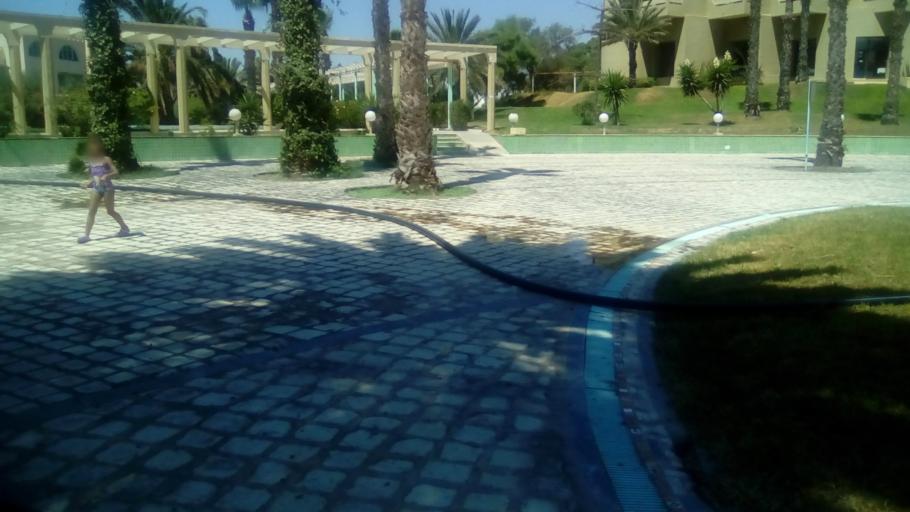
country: TN
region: Nabul
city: Nabeul
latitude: 36.4441
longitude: 10.7371
